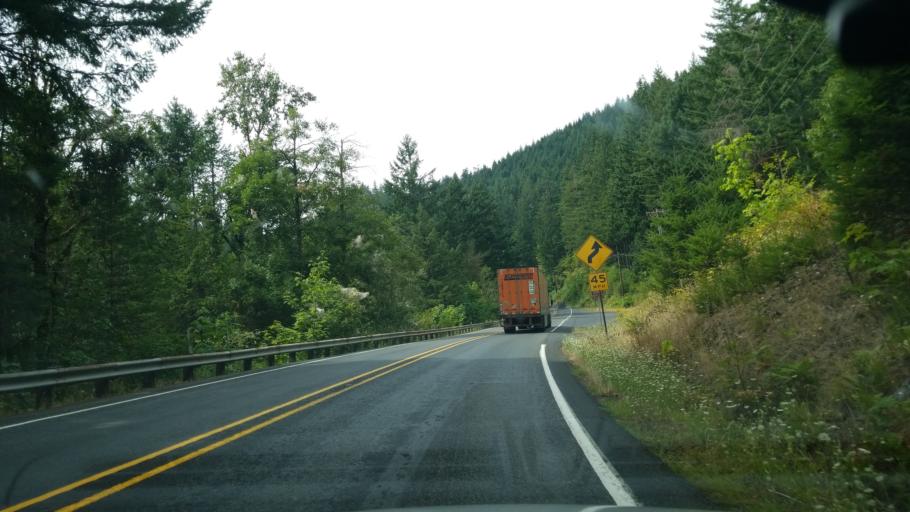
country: US
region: Oregon
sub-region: Hood River County
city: Cascade Locks
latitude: 45.6309
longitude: -122.0115
